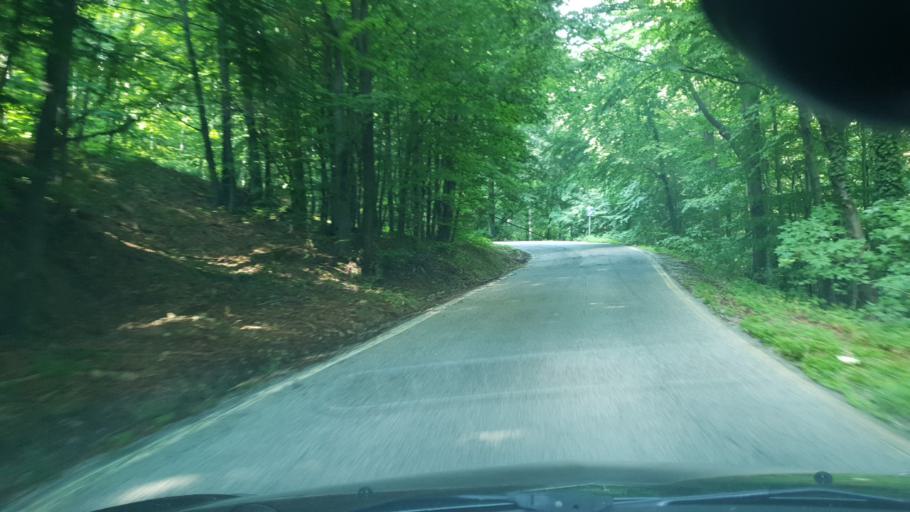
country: HR
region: Grad Zagreb
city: Kasina
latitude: 45.8838
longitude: 15.9759
